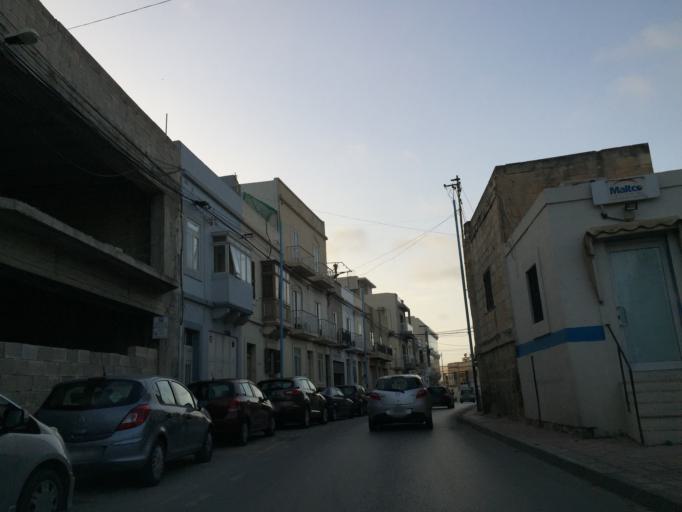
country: MT
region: Saint Paul's Bay
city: San Pawl il-Bahar
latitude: 35.9350
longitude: 14.4143
